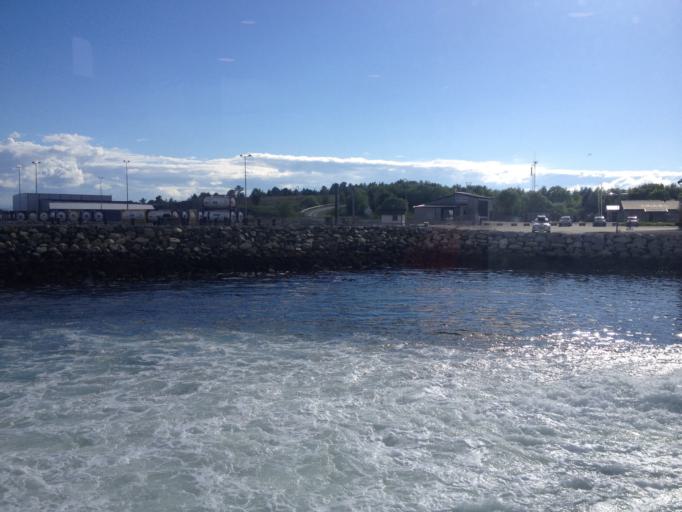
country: NO
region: Sor-Trondelag
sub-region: Hitra
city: Fillan
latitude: 63.5175
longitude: 9.1136
